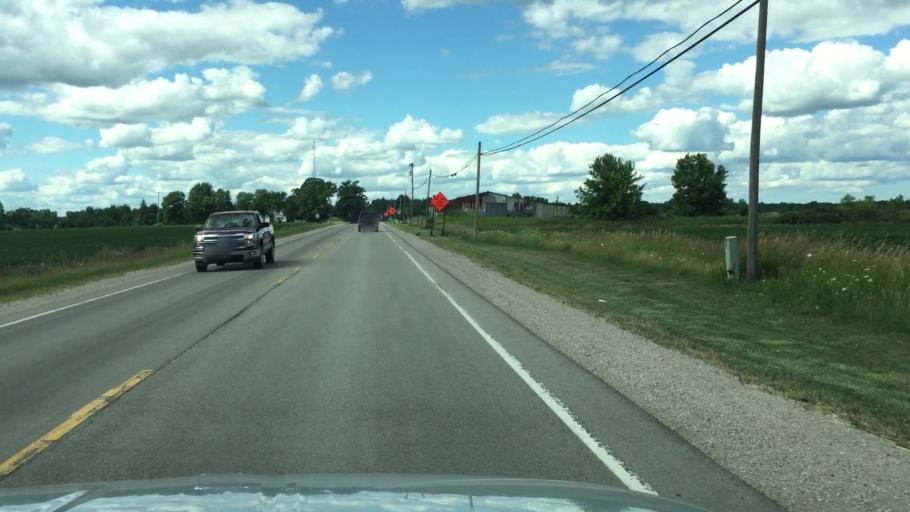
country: US
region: Michigan
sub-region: Saint Clair County
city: Capac
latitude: 42.9993
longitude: -82.9282
